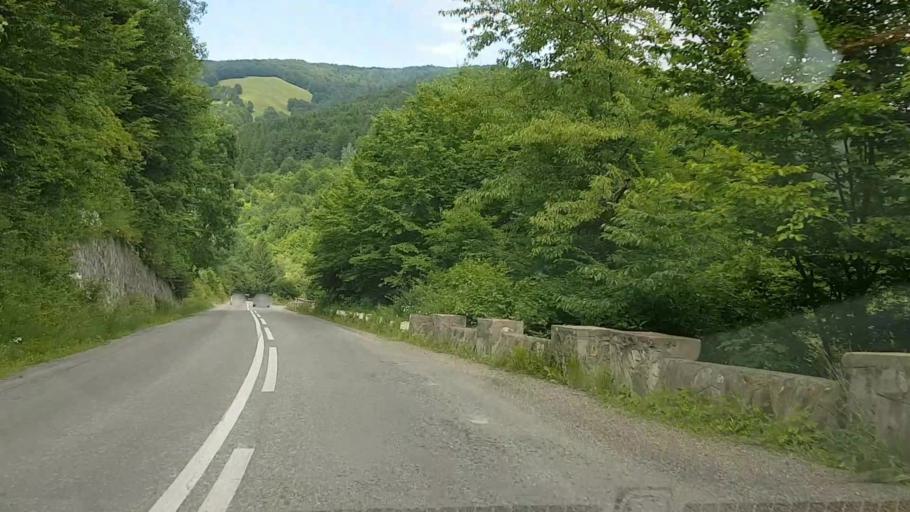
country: RO
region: Neamt
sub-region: Comuna Pangarati
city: Pangarati
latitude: 46.9896
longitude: 26.1169
